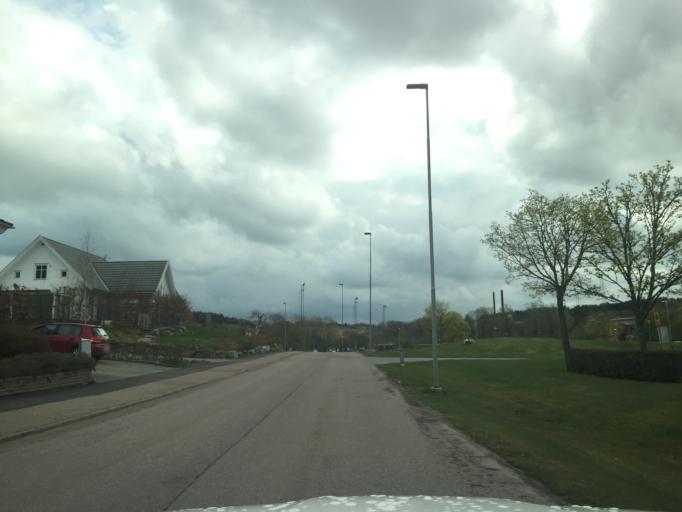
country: SE
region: Vaestra Goetaland
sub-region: Kungalvs Kommun
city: Kungalv
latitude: 57.8906
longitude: 11.9640
